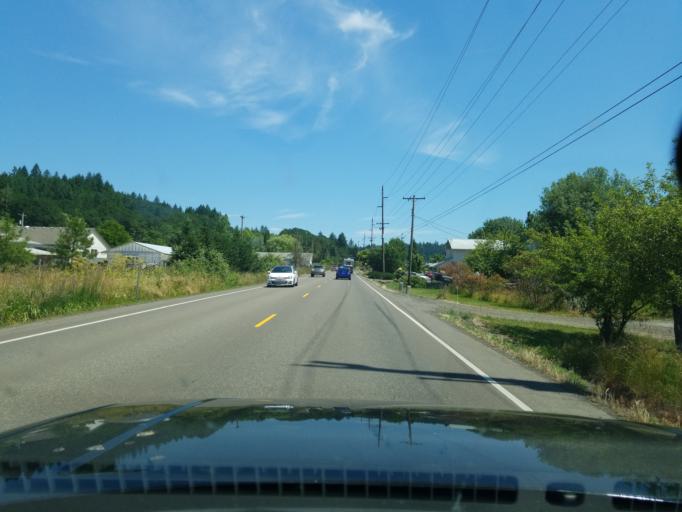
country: US
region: Oregon
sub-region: Yamhill County
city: Yamhill
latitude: 45.3743
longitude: -123.1558
